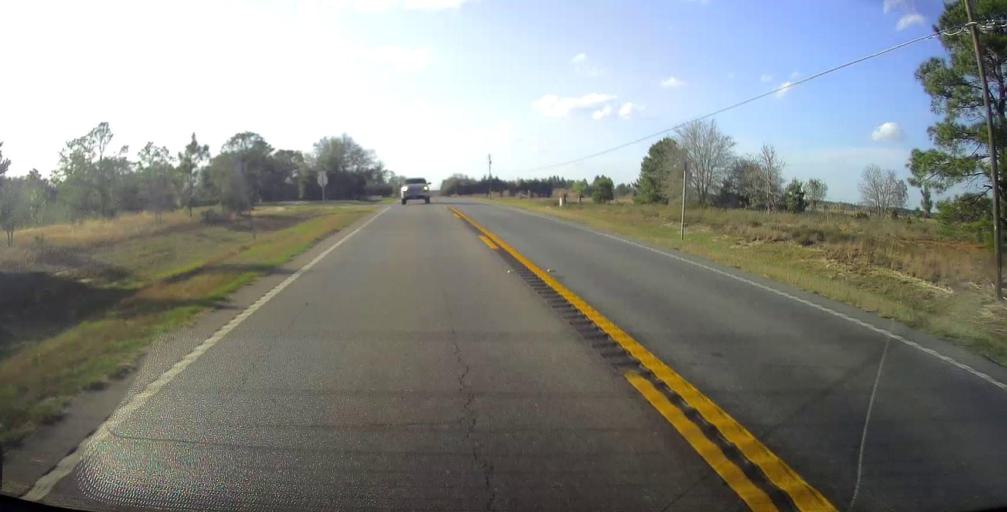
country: US
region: Georgia
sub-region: Tattnall County
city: Reidsville
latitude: 32.0959
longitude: -82.1559
